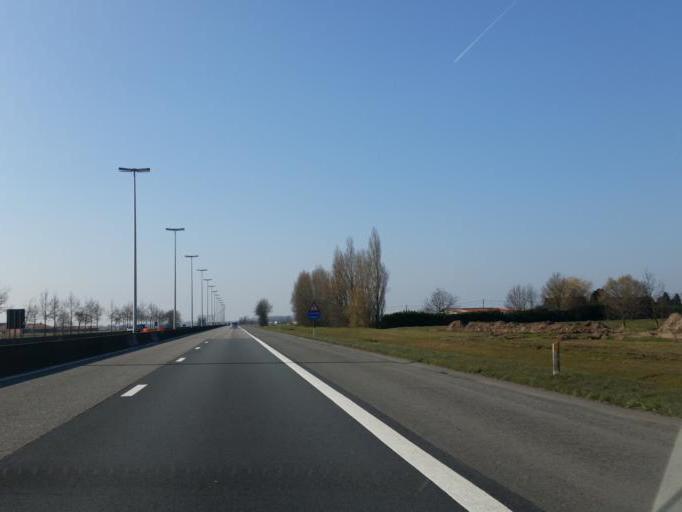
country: BE
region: Flanders
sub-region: Provincie Oost-Vlaanderen
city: Kaprijke
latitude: 51.2091
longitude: 3.6798
